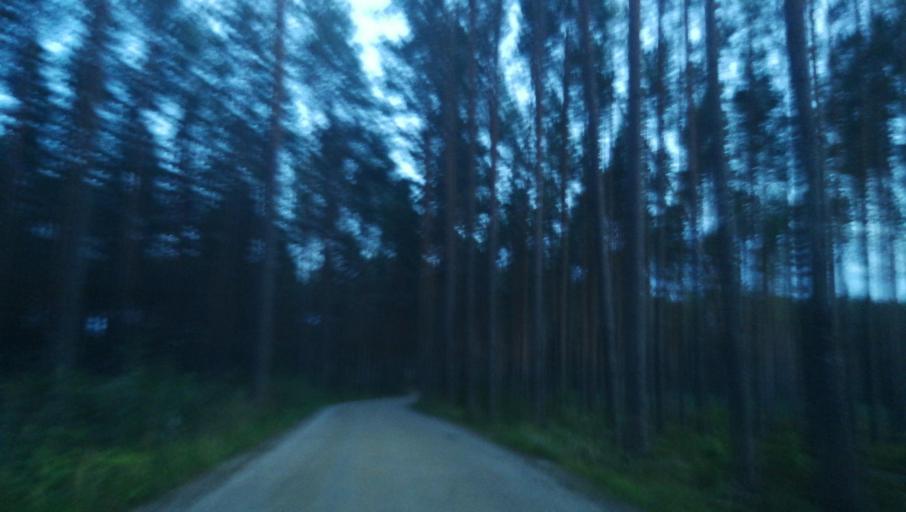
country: LV
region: Valmieras Rajons
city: Valmiera
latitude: 57.5142
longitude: 25.4092
